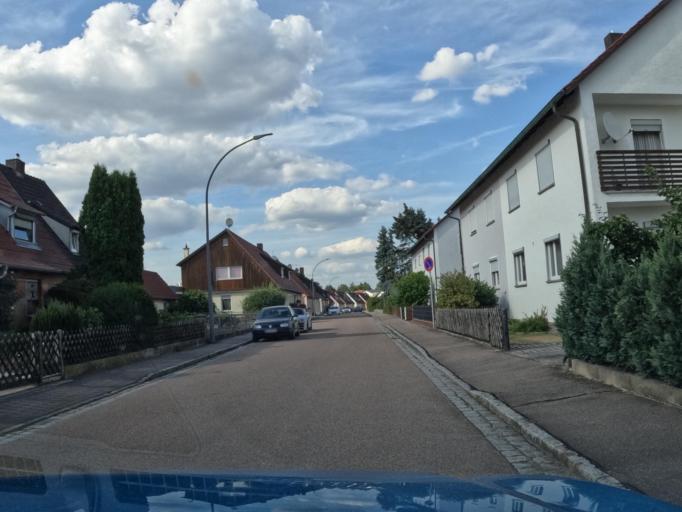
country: DE
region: Bavaria
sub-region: Upper Palatinate
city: Schwarzenfeld
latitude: 49.3841
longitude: 12.1222
